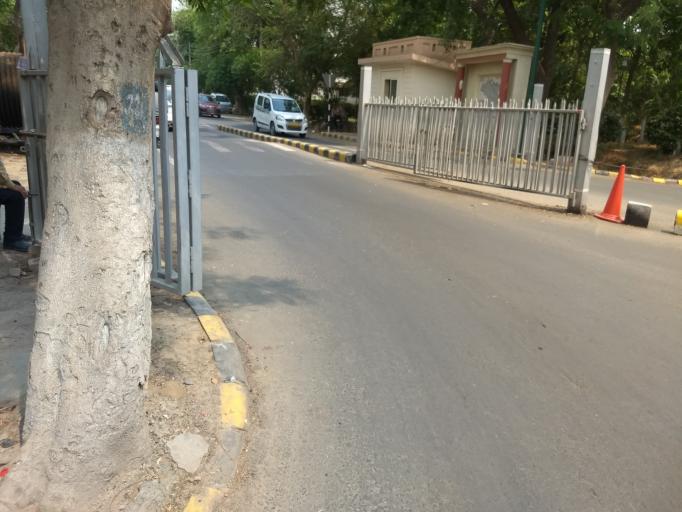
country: IN
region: Haryana
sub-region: Gurgaon
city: Gurgaon
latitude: 28.4673
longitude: 77.0949
